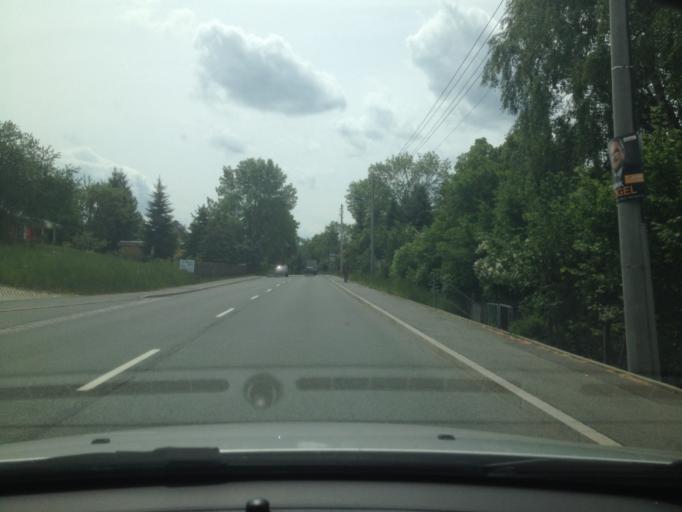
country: DE
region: Saxony
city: Stollberg
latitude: 50.6896
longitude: 12.7655
